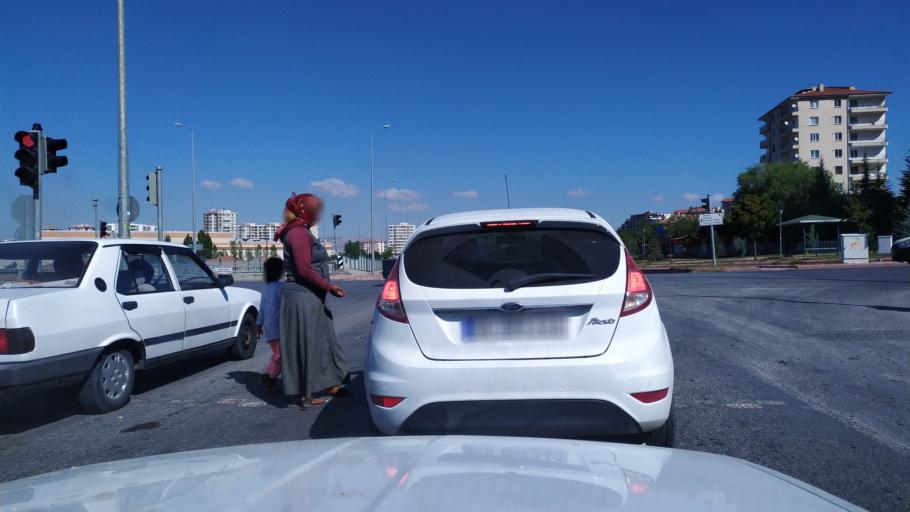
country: TR
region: Kayseri
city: Kocasinan
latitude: 38.7376
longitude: 35.5450
